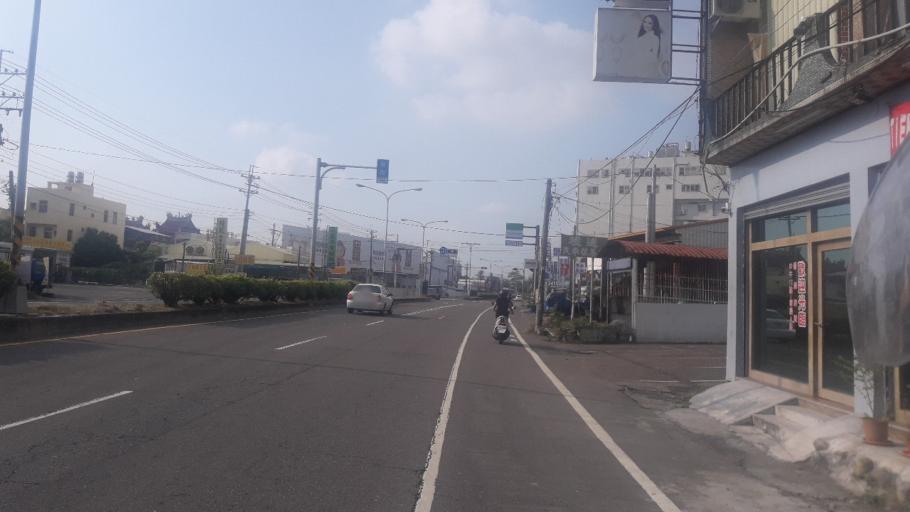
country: TW
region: Taiwan
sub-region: Tainan
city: Tainan
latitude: 22.8642
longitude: 120.2574
